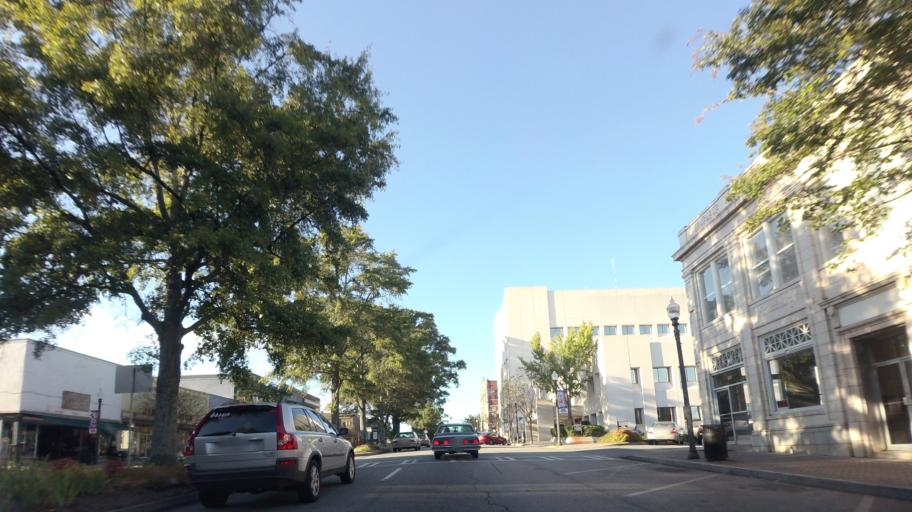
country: US
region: Georgia
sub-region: Spalding County
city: Griffin
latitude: 33.2477
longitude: -84.2638
